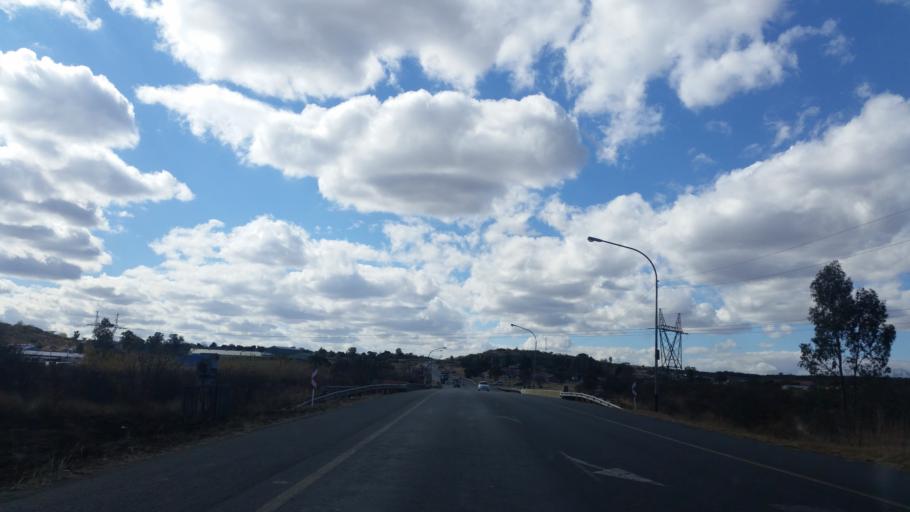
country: ZA
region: KwaZulu-Natal
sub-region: uThukela District Municipality
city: Ladysmith
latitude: -28.5386
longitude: 29.7983
